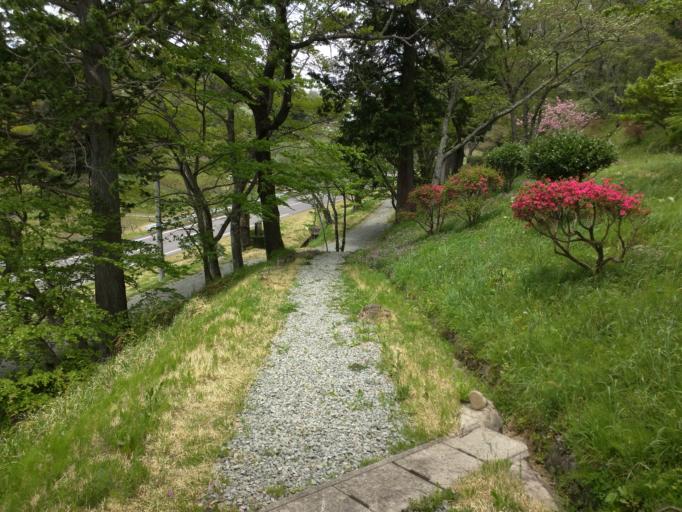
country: JP
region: Fukushima
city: Nihommatsu
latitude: 37.5993
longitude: 140.4272
